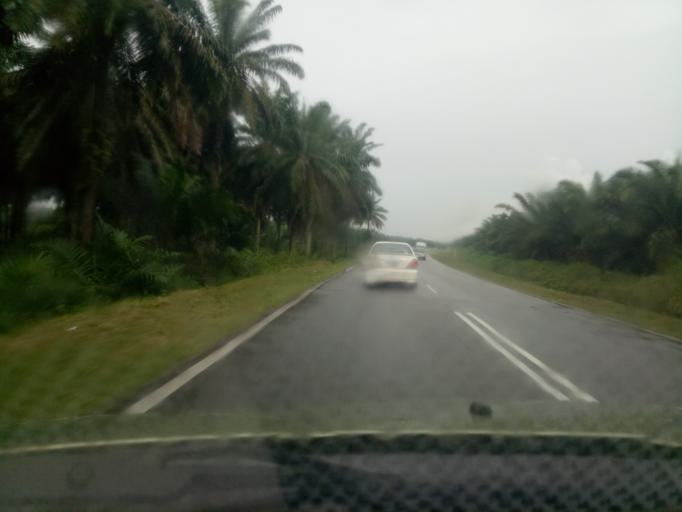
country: MY
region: Penang
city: Tasek Glugor
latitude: 5.5074
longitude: 100.5740
